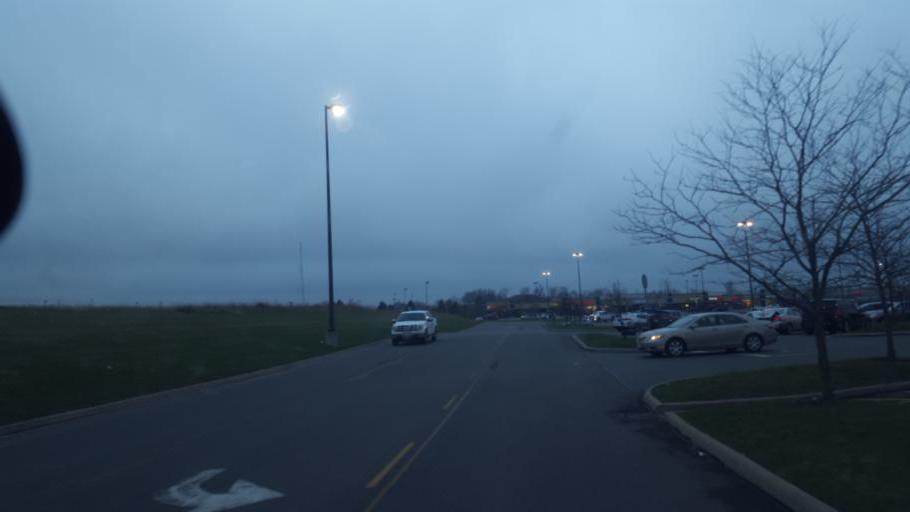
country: US
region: Ohio
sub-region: Ashland County
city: Ashland
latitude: 40.8610
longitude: -82.2719
